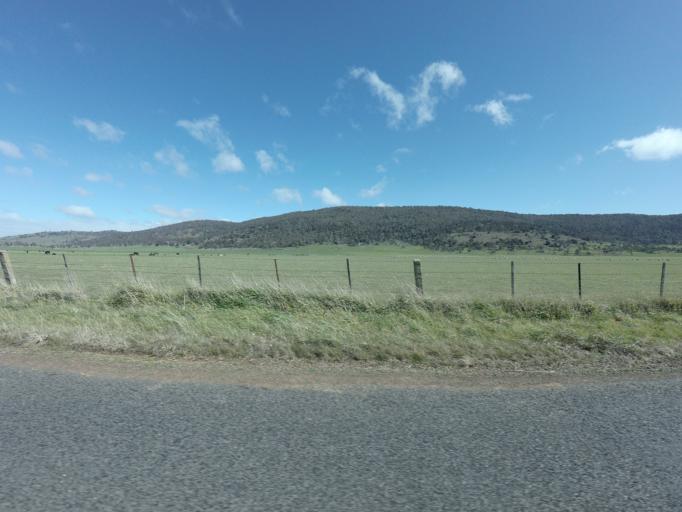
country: AU
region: Tasmania
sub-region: Northern Midlands
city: Evandale
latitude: -41.9734
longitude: 147.4444
